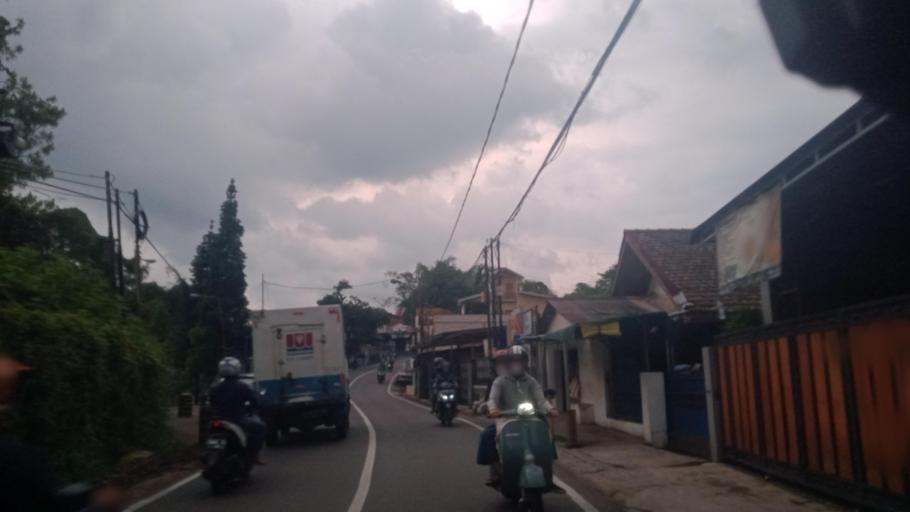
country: ID
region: West Java
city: Lembang
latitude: -6.8532
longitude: 107.5916
